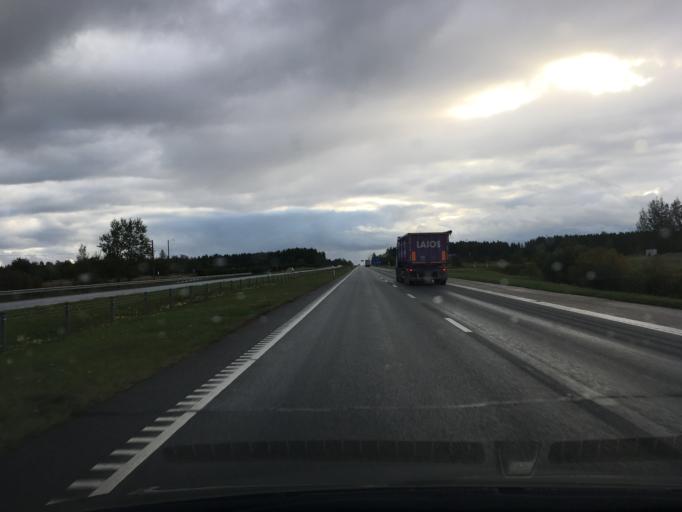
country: EE
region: Harju
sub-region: Kuusalu vald
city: Kuusalu
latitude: 59.4469
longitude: 25.4016
